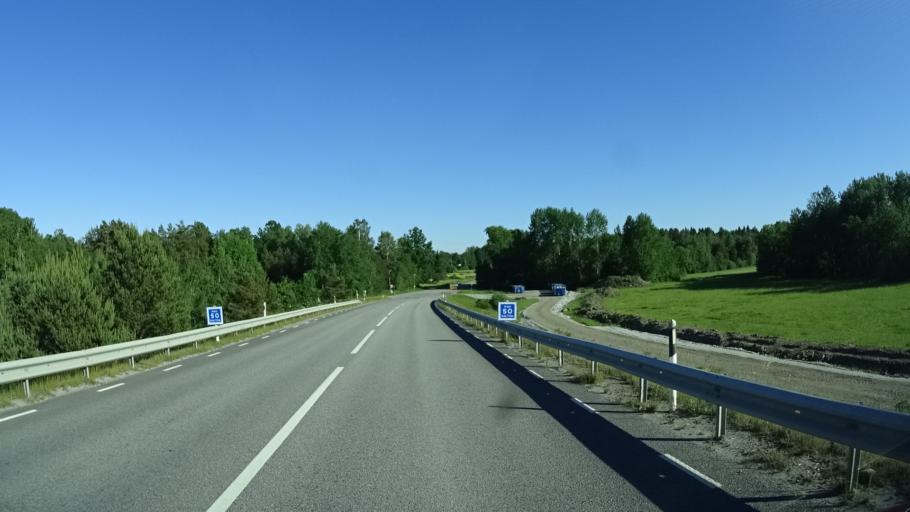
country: SE
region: Stockholm
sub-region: Vallentuna Kommun
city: Vallentuna
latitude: 59.5684
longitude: 18.0997
